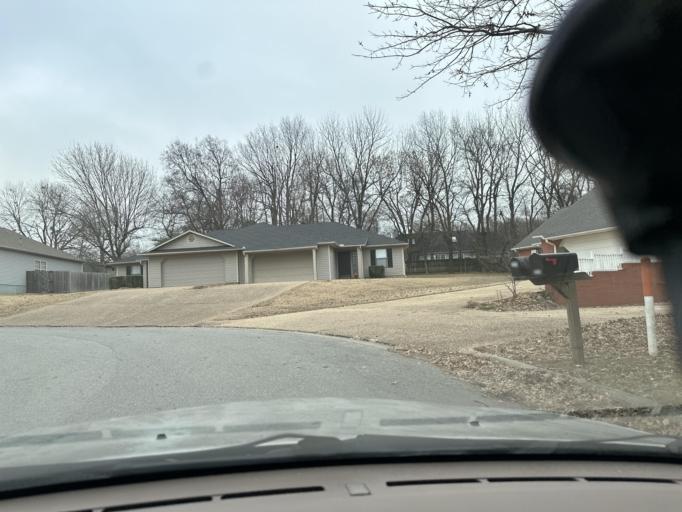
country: US
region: Arkansas
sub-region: Washington County
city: Fayetteville
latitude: 36.0840
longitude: -94.1177
